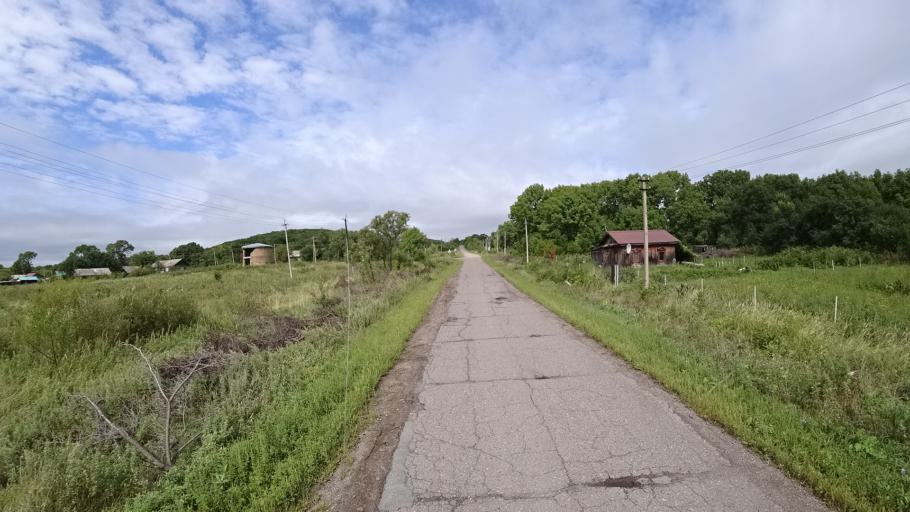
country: RU
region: Primorskiy
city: Lyalichi
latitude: 44.1369
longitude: 132.3876
